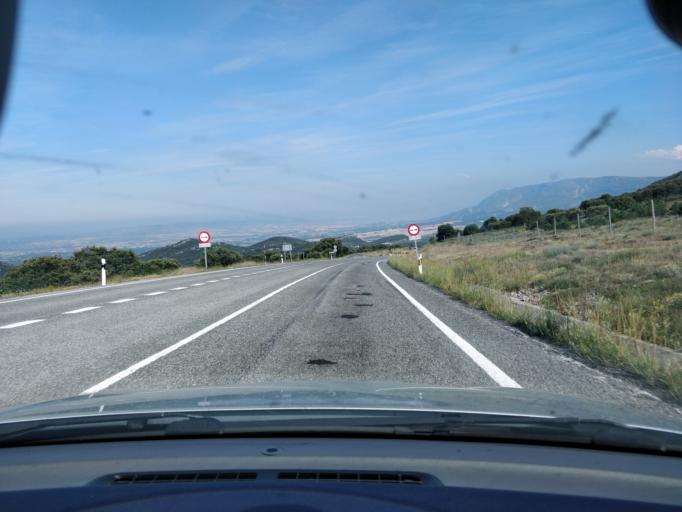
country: ES
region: Castille and Leon
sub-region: Provincia de Burgos
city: Medina de Pomar
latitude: 42.9253
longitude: -3.6324
